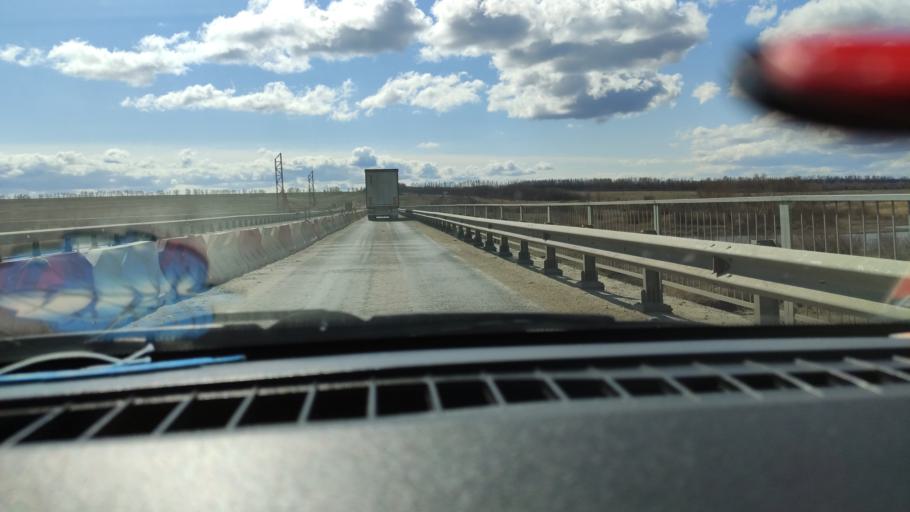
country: RU
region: Saratov
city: Dukhovnitskoye
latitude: 52.7356
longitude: 48.2563
